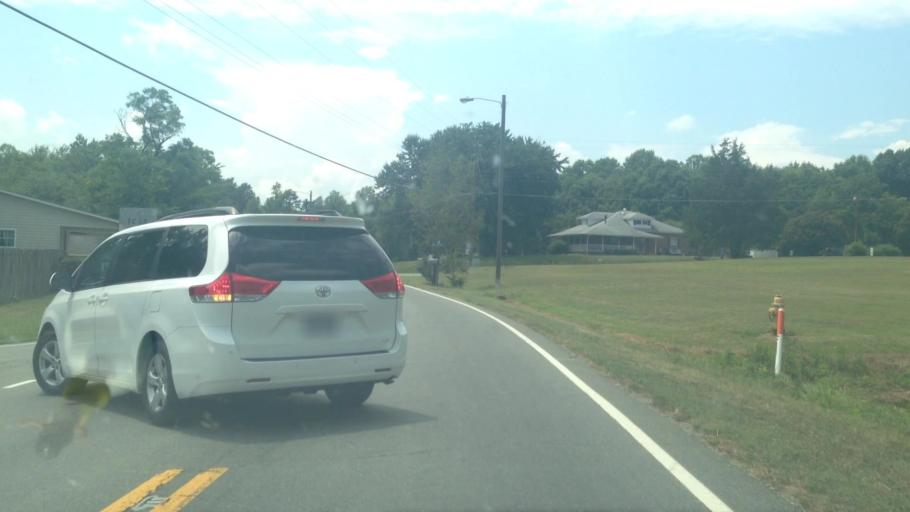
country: US
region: North Carolina
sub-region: Forsyth County
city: Walkertown
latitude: 36.1782
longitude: -80.1776
